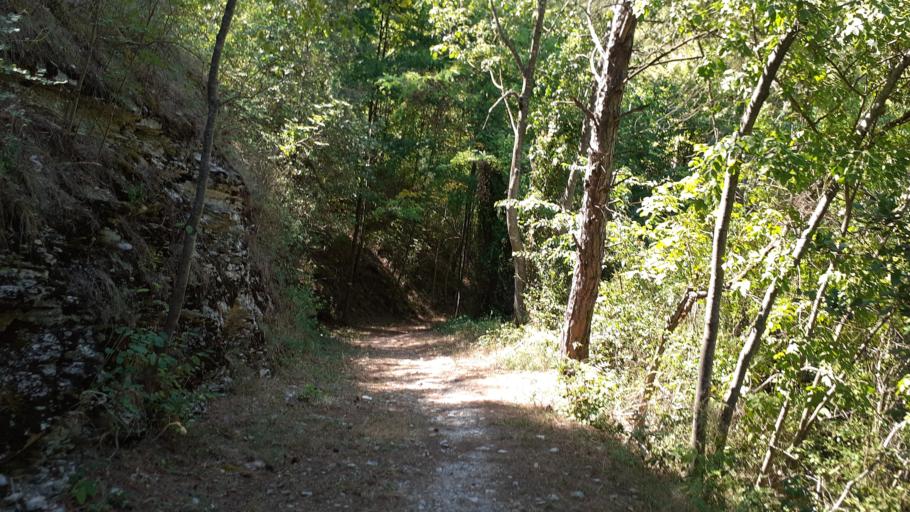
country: IT
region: Abruzzo
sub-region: Provincia di Pescara
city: San Valentino in Abruzzo Citeriore
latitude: 42.2435
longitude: 13.9681
